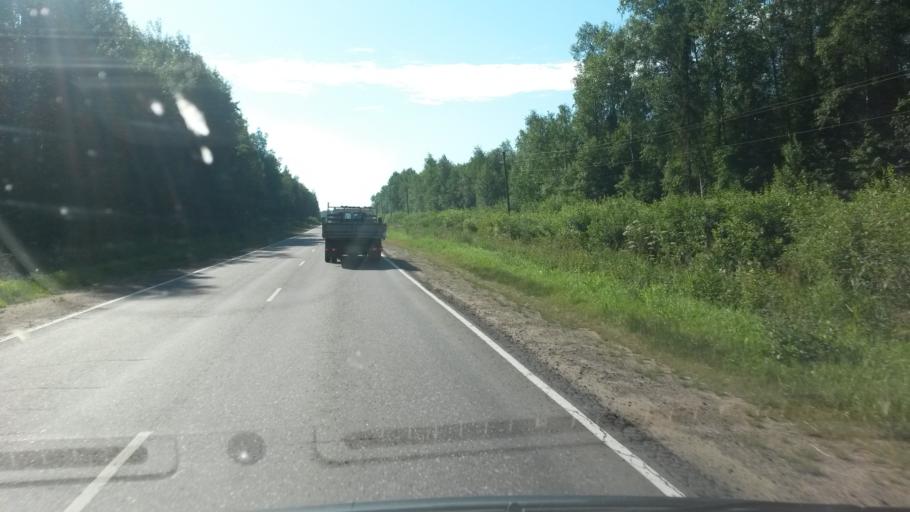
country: RU
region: Ivanovo
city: Pistsovo
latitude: 57.1329
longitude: 40.5893
